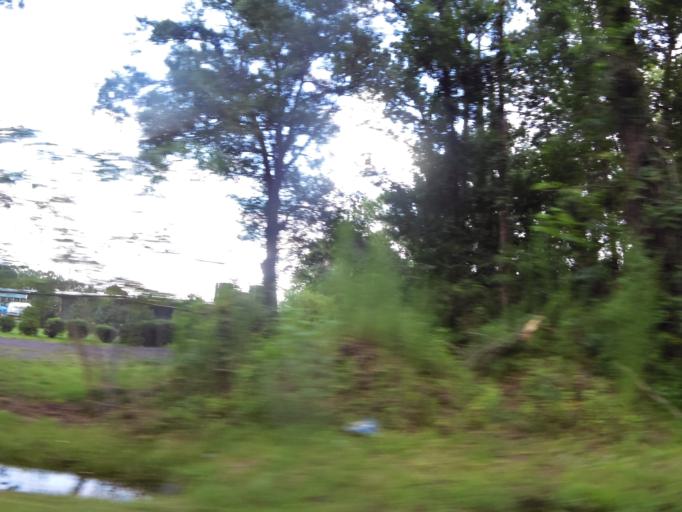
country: US
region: Florida
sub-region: Duval County
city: Jacksonville
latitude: 30.3192
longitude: -81.7667
